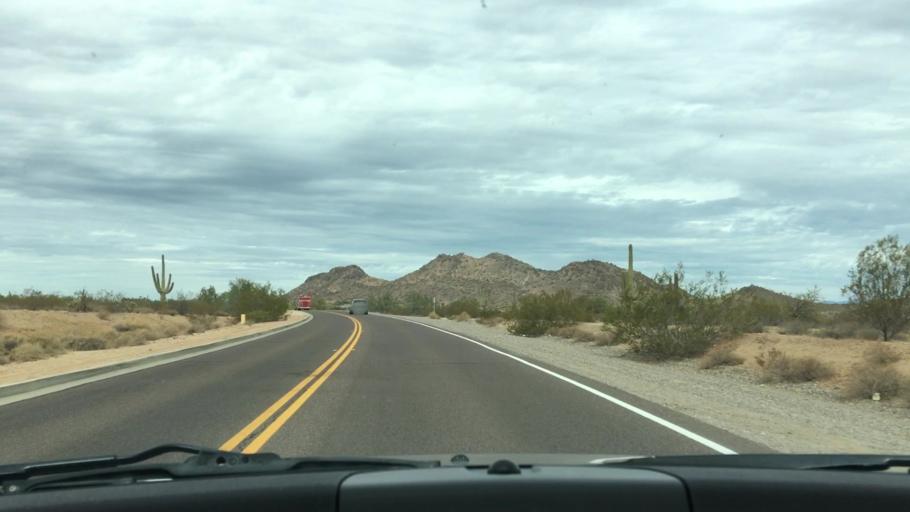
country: US
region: Arizona
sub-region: Maricopa County
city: Sun City West
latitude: 33.7201
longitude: -112.2341
